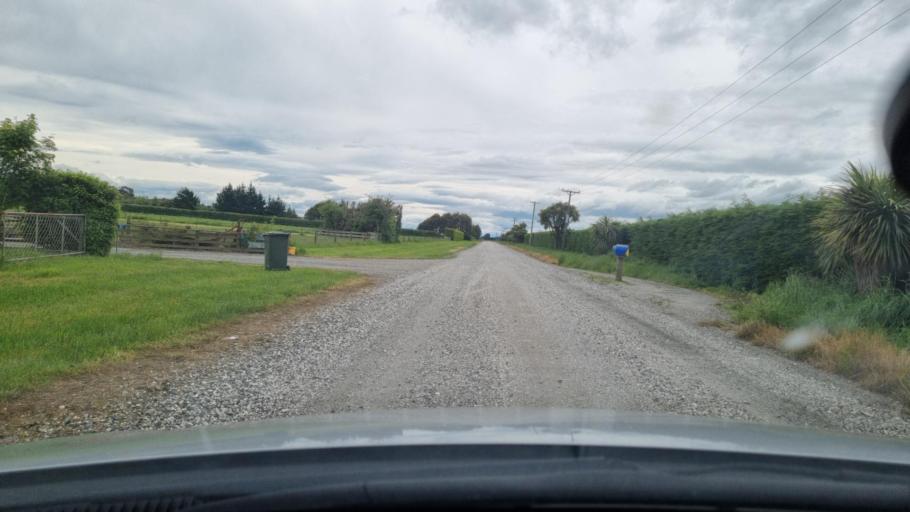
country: NZ
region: Southland
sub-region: Invercargill City
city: Invercargill
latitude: -46.3755
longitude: 168.2988
